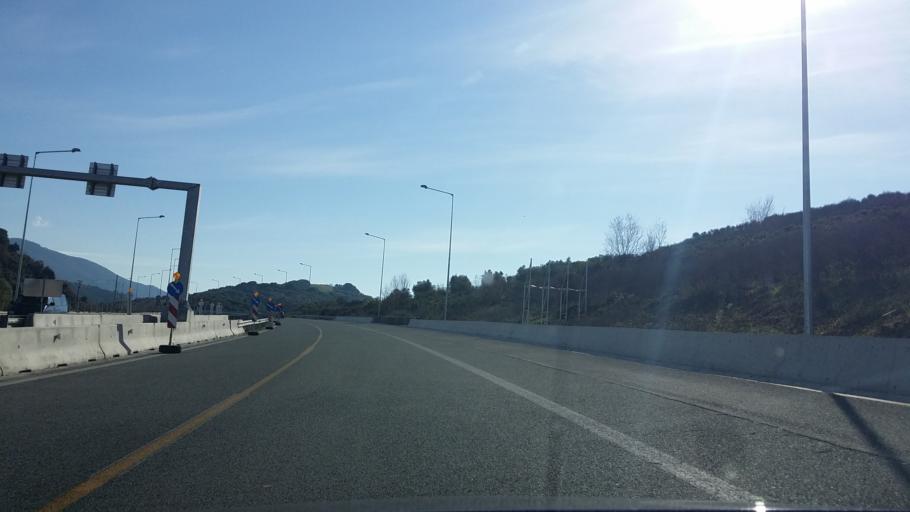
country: GR
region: West Greece
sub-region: Nomos Aitolias kai Akarnanias
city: Angelokastro
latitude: 38.5460
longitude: 21.2740
